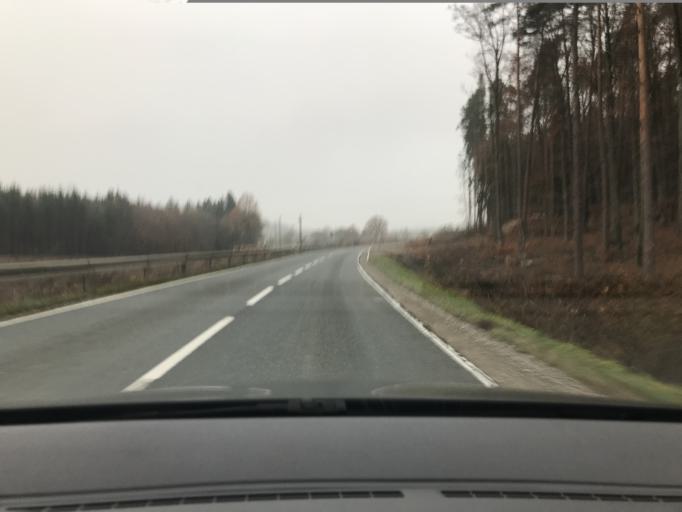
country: DE
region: Bavaria
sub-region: Regierungsbezirk Mittelfranken
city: Wilburgstetten
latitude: 48.9966
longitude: 10.4148
